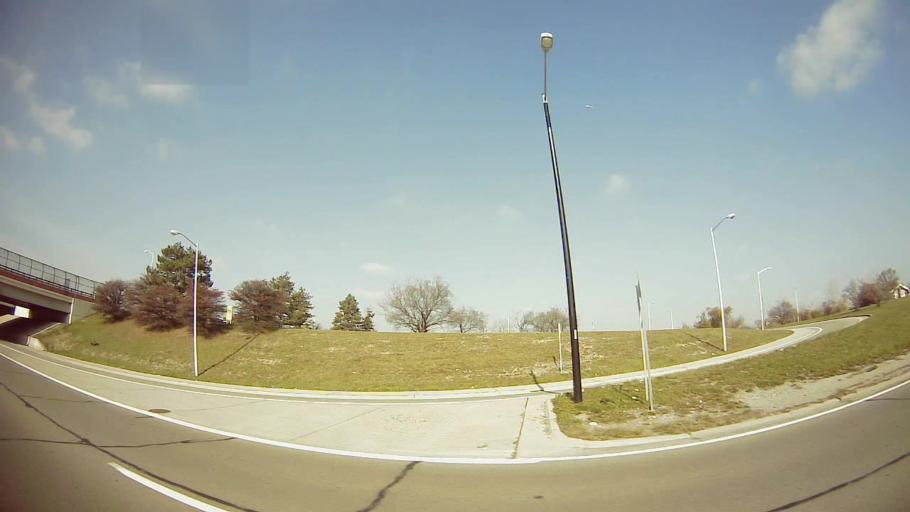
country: US
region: Michigan
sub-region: Wayne County
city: Dearborn Heights
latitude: 42.3288
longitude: -83.2348
